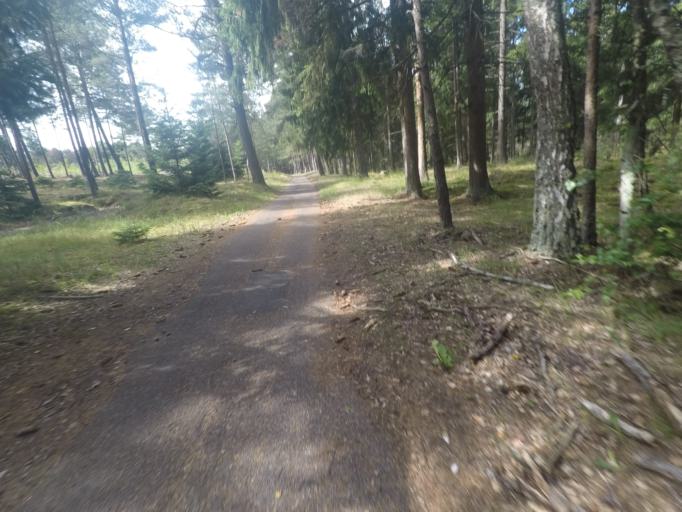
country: LT
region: Klaipedos apskritis
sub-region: Klaipeda
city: Klaipeda
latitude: 55.6156
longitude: 21.1237
